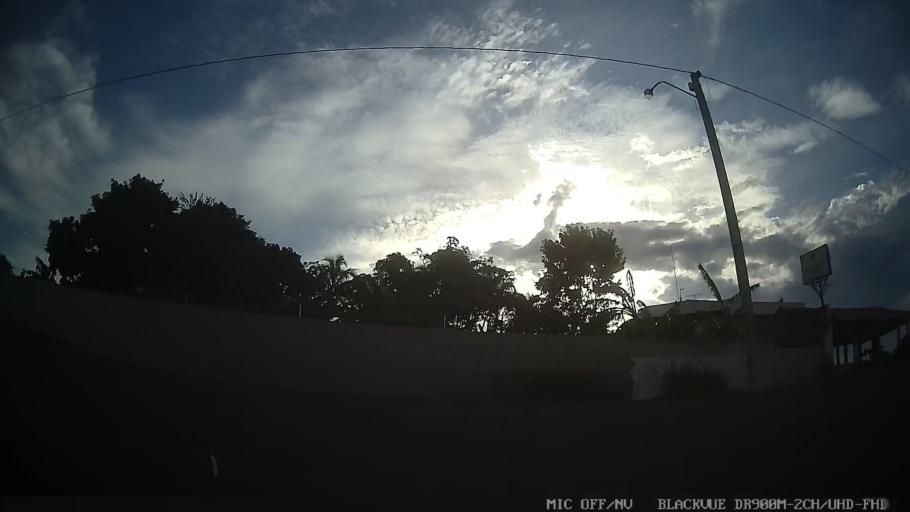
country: BR
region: Sao Paulo
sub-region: Tiete
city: Tiete
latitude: -23.0830
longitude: -47.7206
